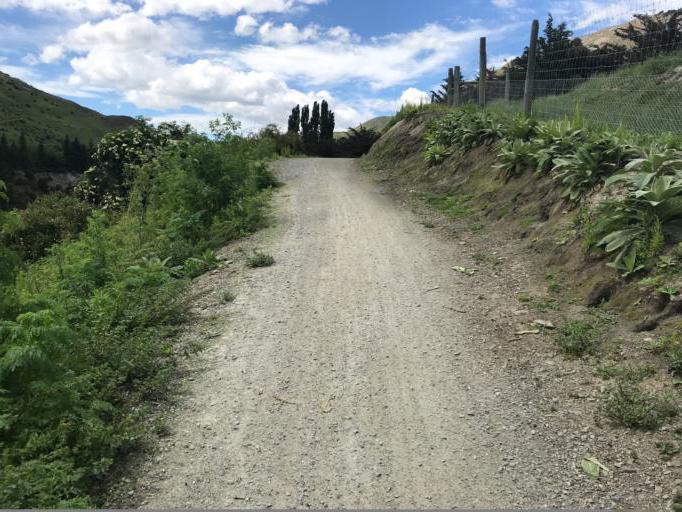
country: NZ
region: Otago
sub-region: Queenstown-Lakes District
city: Arrowtown
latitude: -44.9990
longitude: 168.8692
